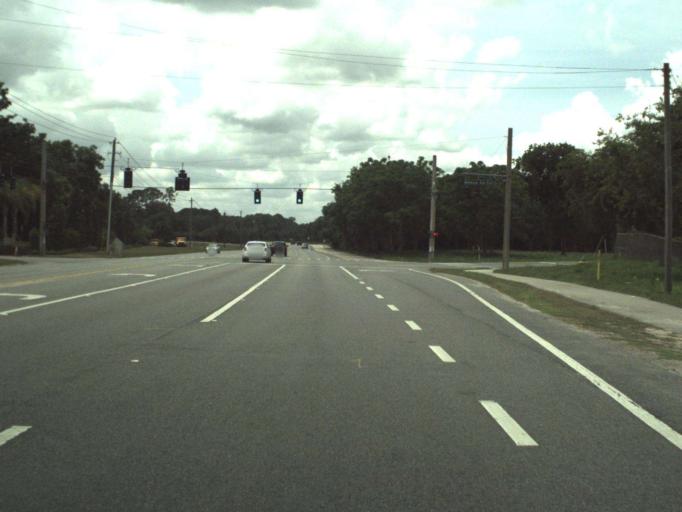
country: US
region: Florida
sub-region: Volusia County
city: Daytona Beach
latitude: 29.1812
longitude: -81.0424
